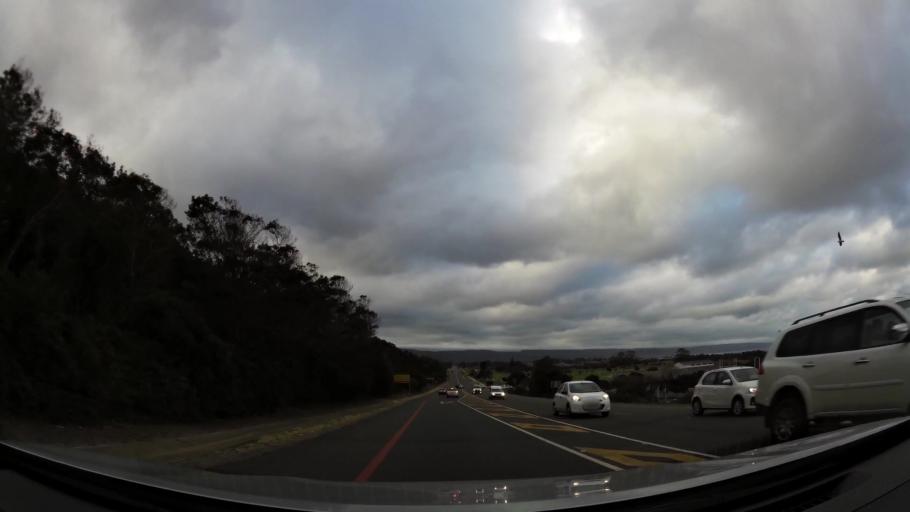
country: ZA
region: Western Cape
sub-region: Eden District Municipality
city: Plettenberg Bay
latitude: -34.0413
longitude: 23.3692
